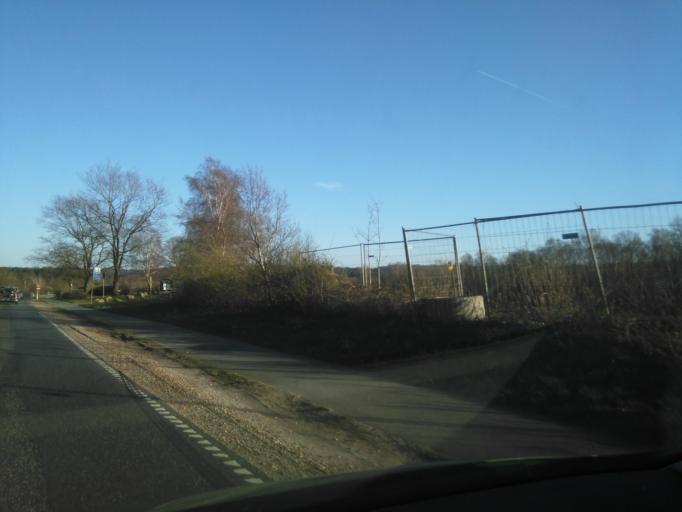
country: DK
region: Central Jutland
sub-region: Silkeborg Kommune
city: Silkeborg
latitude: 56.1770
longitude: 9.5958
